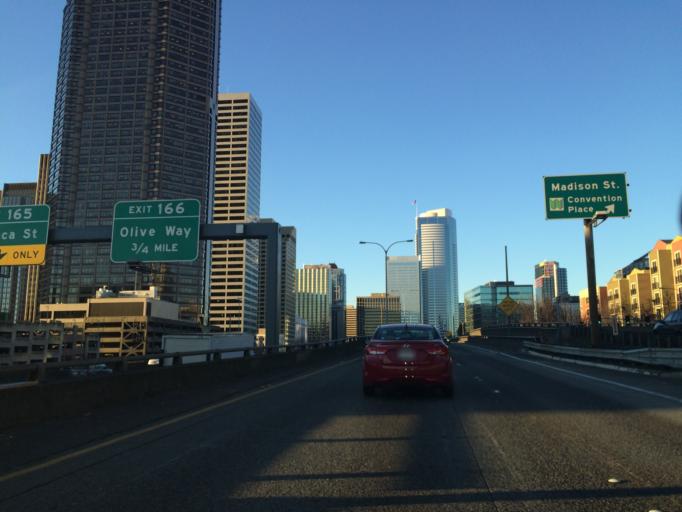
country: US
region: Washington
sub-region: King County
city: Seattle
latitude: 47.6039
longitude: -122.3268
